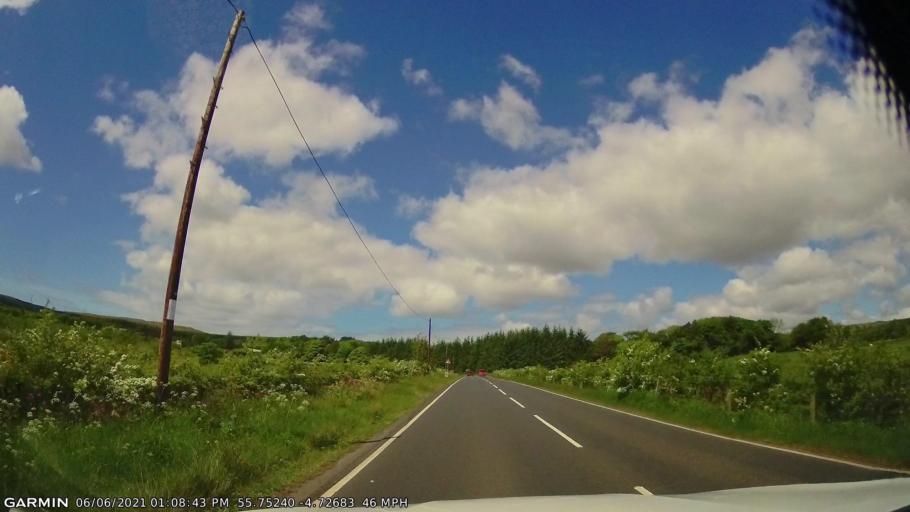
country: GB
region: Scotland
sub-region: North Ayrshire
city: Kilbirnie
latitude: 55.7524
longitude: -4.7268
